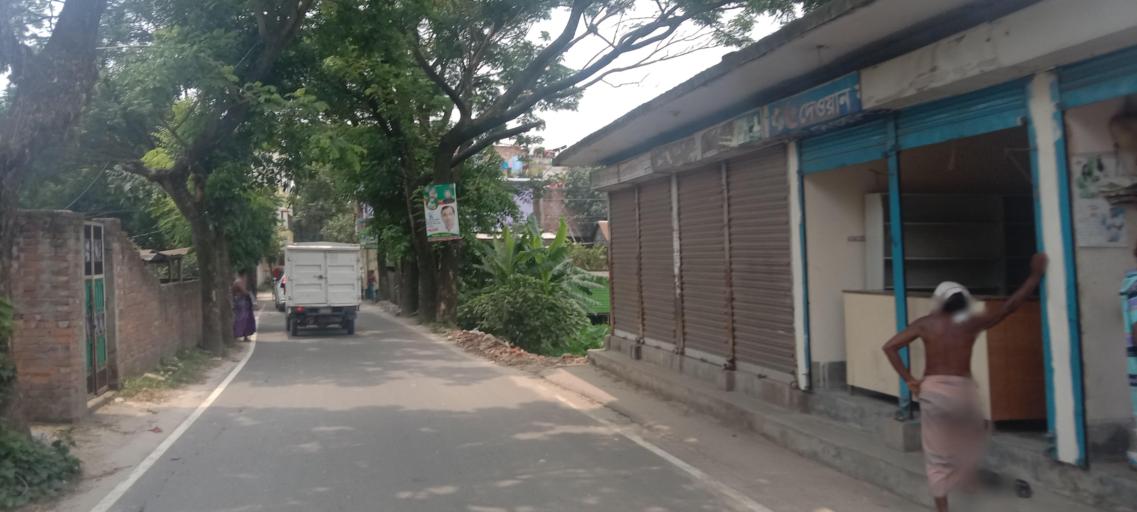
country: BD
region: Dhaka
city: Azimpur
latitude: 23.7175
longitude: 90.3448
